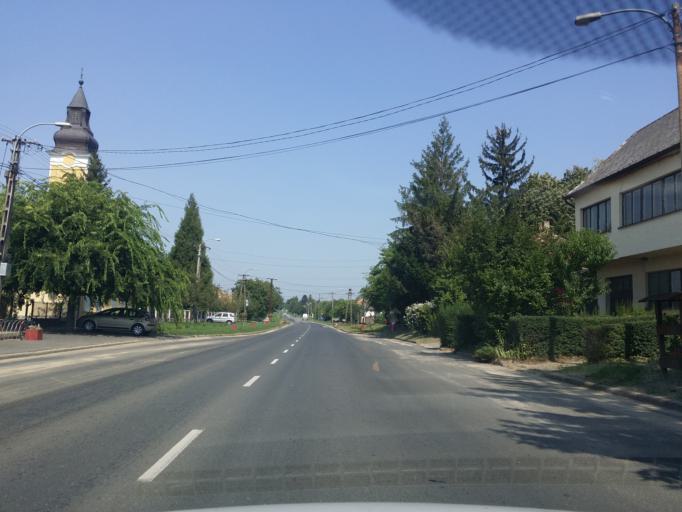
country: HU
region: Tolna
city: Pincehely
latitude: 46.7159
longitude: 18.4769
